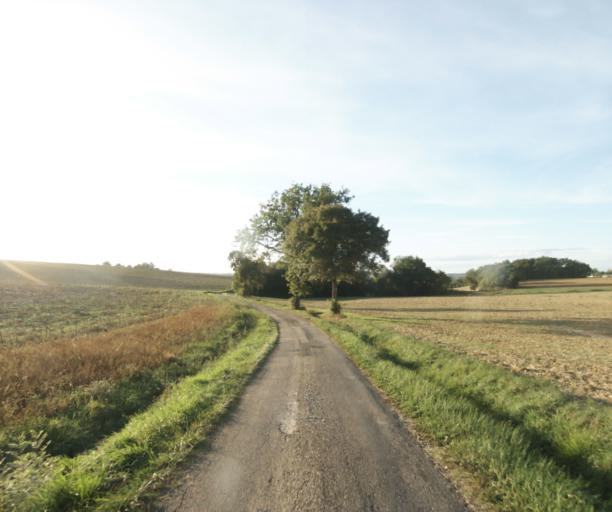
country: FR
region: Midi-Pyrenees
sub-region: Departement du Gers
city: Gondrin
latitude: 43.8766
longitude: 0.3053
